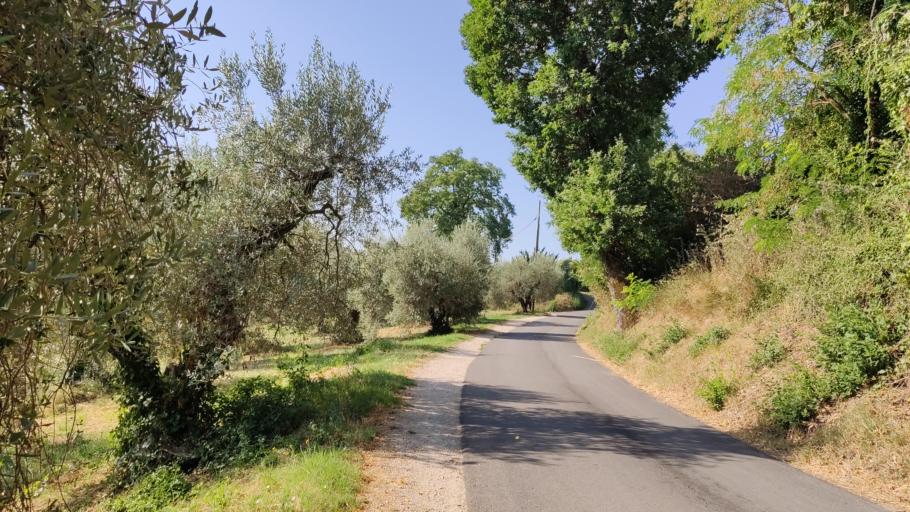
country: IT
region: Umbria
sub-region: Provincia di Terni
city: Amelia
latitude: 42.5407
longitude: 12.4122
